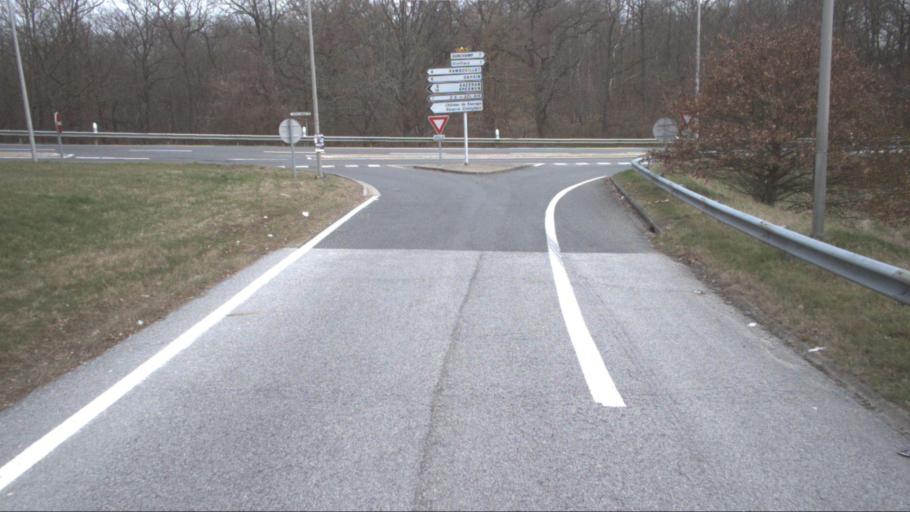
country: FR
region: Ile-de-France
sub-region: Departement des Yvelines
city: Rambouillet
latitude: 48.6198
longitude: 1.8323
